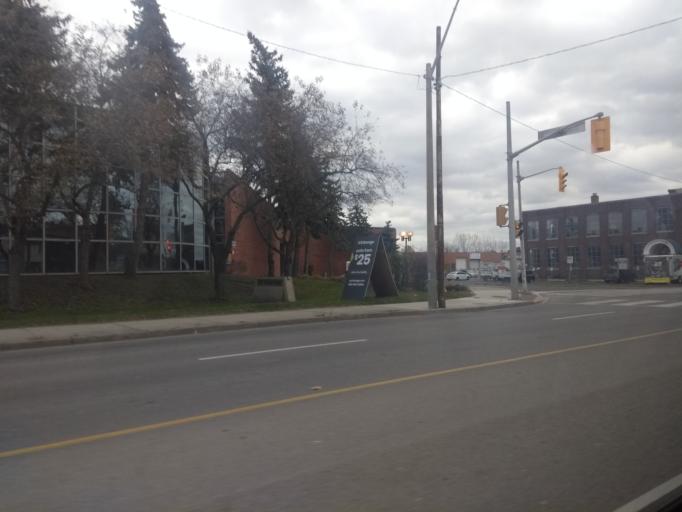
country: CA
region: Ontario
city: Toronto
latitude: 43.6774
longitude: -79.4722
